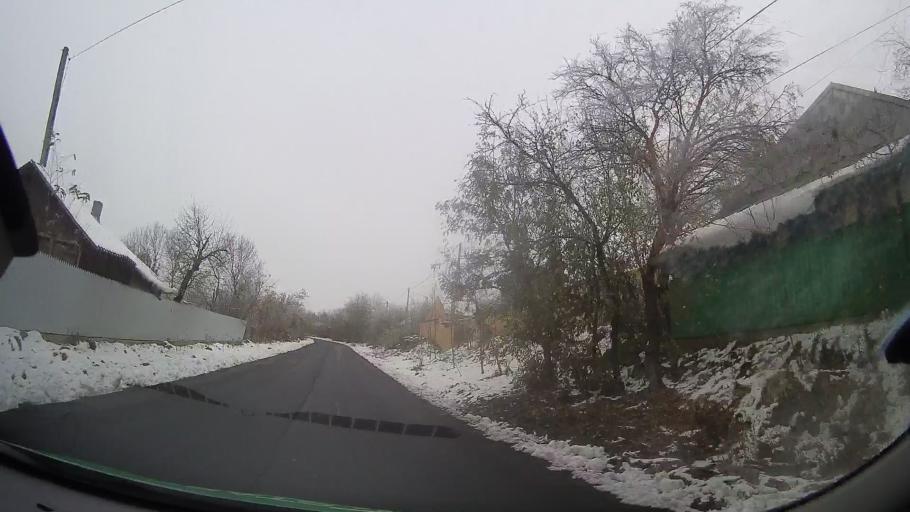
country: RO
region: Vaslui
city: Coroiesti
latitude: 46.2109
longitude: 27.4418
